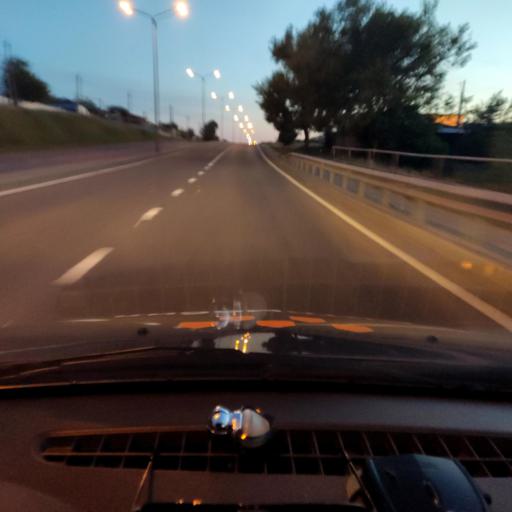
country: RU
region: Belgorod
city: Gubkin
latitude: 51.2683
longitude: 37.5659
